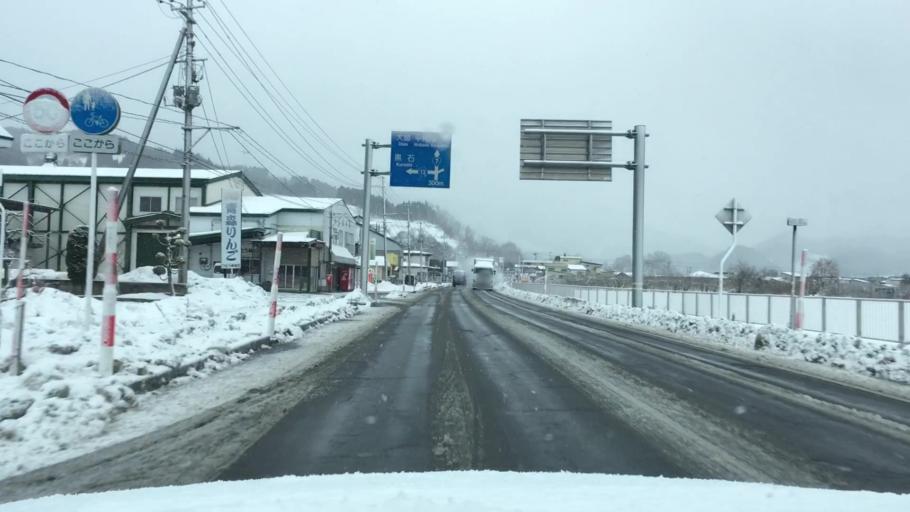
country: JP
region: Aomori
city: Hirosaki
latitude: 40.5406
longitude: 140.5538
